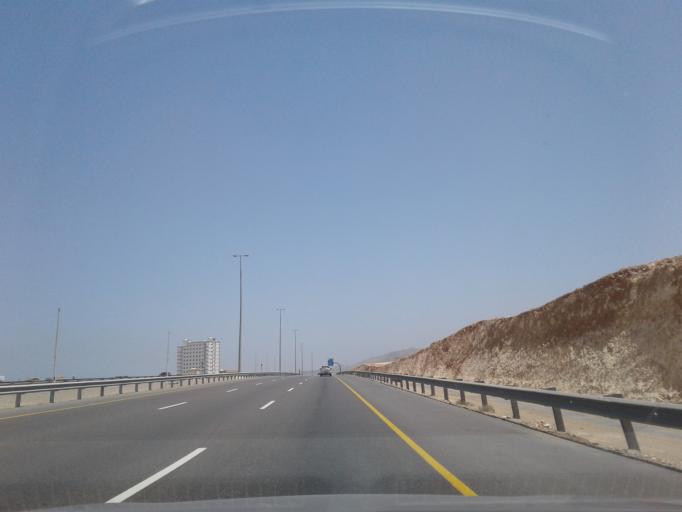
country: OM
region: Muhafazat Masqat
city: Bawshar
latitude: 23.5663
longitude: 58.3668
